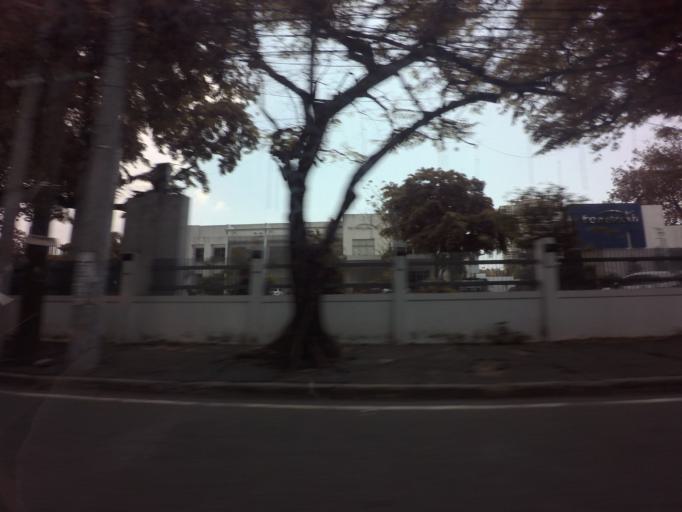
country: PH
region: Metro Manila
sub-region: Makati City
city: Makati City
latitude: 14.5633
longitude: 121.0390
